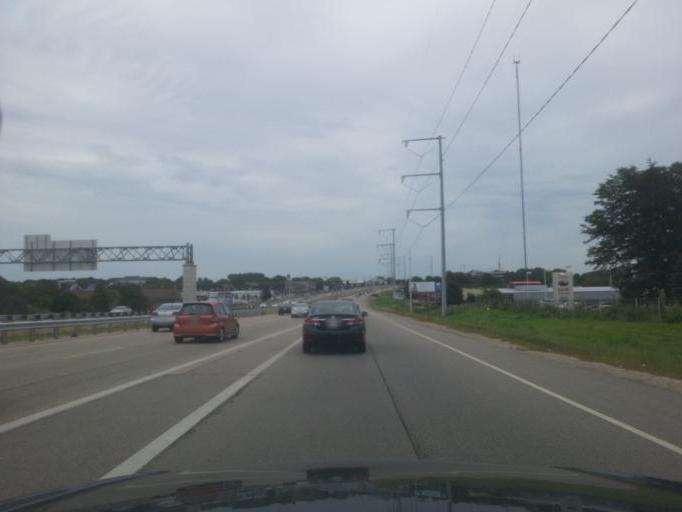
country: US
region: Wisconsin
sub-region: Dane County
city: Middleton
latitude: 43.0531
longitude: -89.4988
